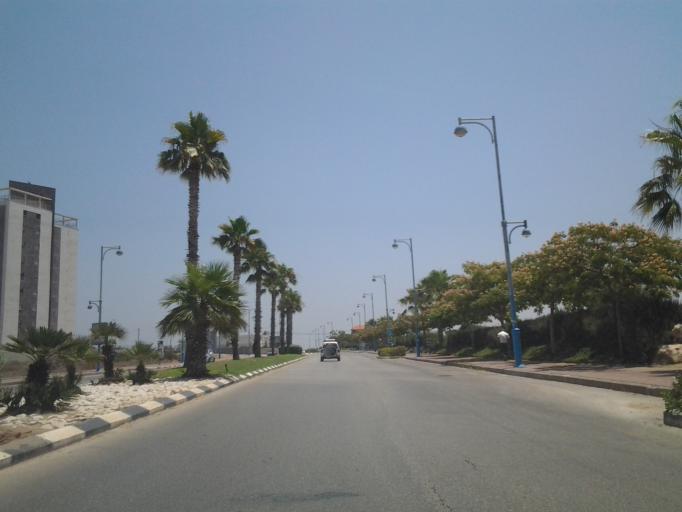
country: IL
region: Haifa
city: Hadera
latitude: 32.4439
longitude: 34.8881
